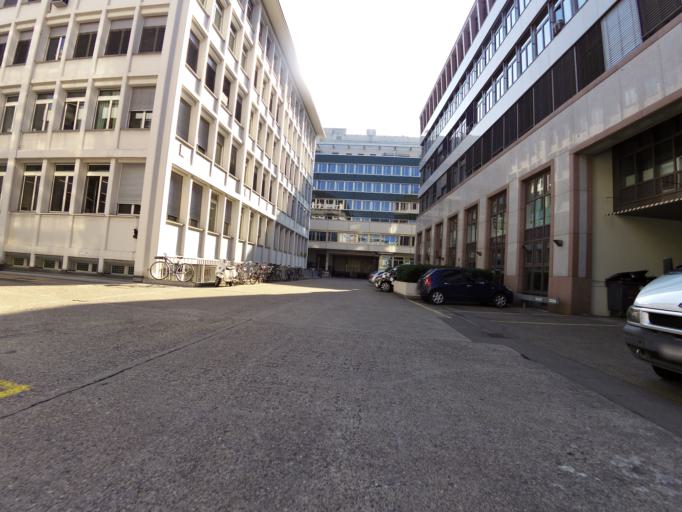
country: CH
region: Zurich
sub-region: Bezirk Zuerich
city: Zuerich (Kreis 5) / Escher-Wyss
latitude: 47.3925
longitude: 8.5105
